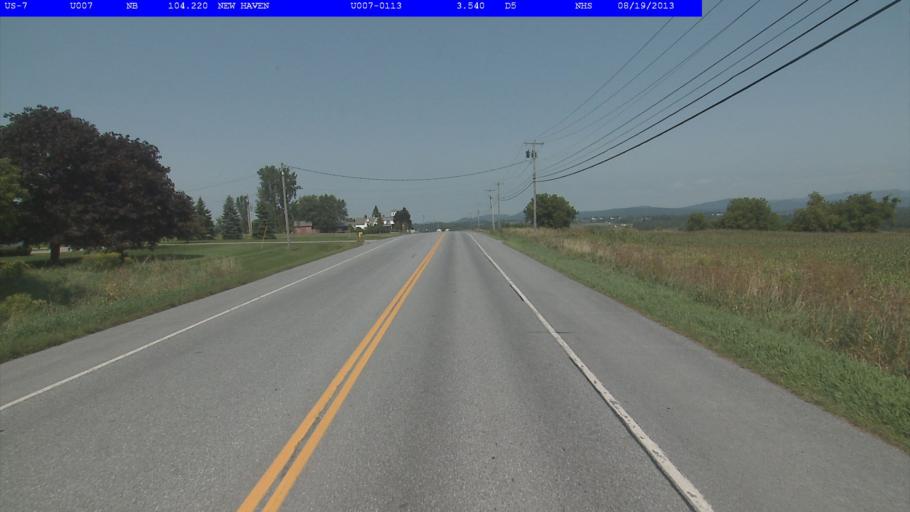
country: US
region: Vermont
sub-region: Addison County
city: Middlebury (village)
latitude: 44.0964
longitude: -73.1734
